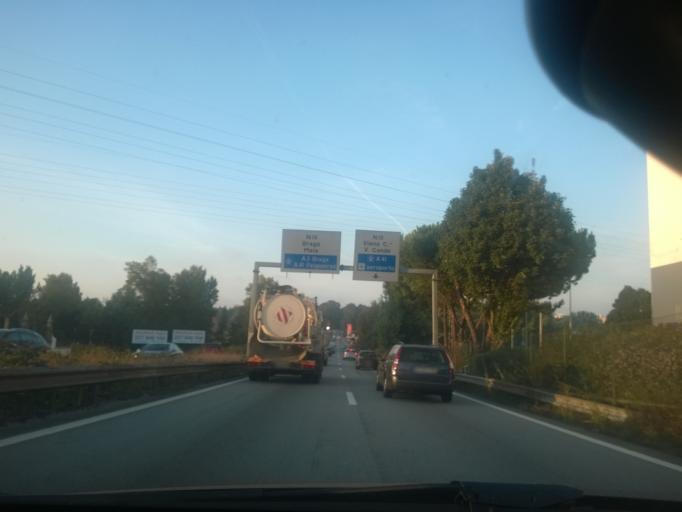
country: PT
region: Porto
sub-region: Maia
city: Leca do Bailio
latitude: 41.2160
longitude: -8.6270
